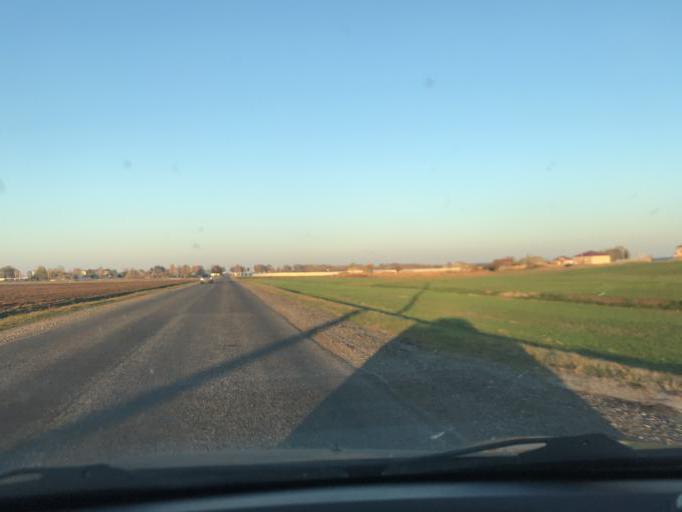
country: BY
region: Gomel
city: Brahin
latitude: 51.8013
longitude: 30.2691
